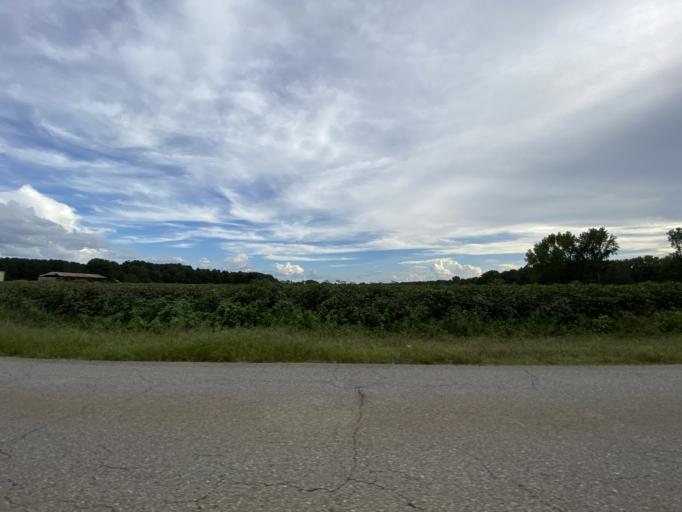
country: US
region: Alabama
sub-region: Madison County
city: Hazel Green
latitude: 34.9032
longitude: -86.6530
